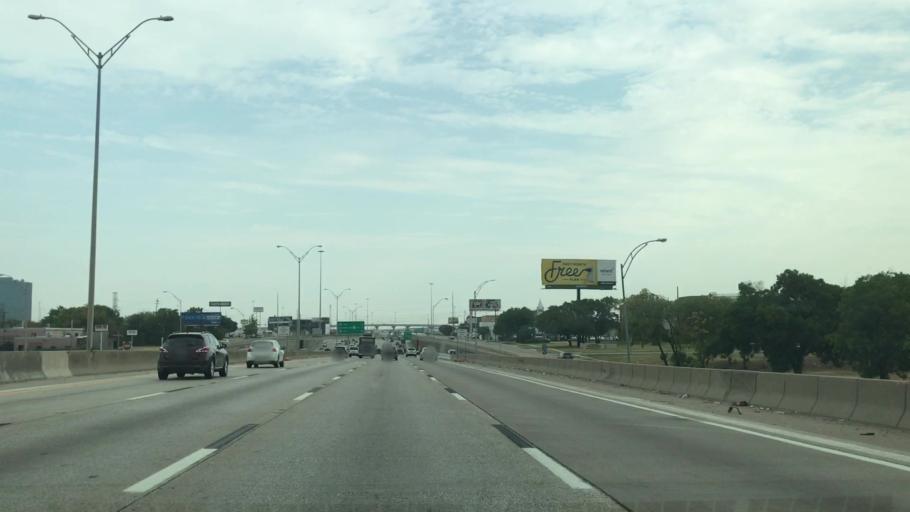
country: US
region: Texas
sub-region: Tarrant County
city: Fort Worth
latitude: 32.7339
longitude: -97.3203
